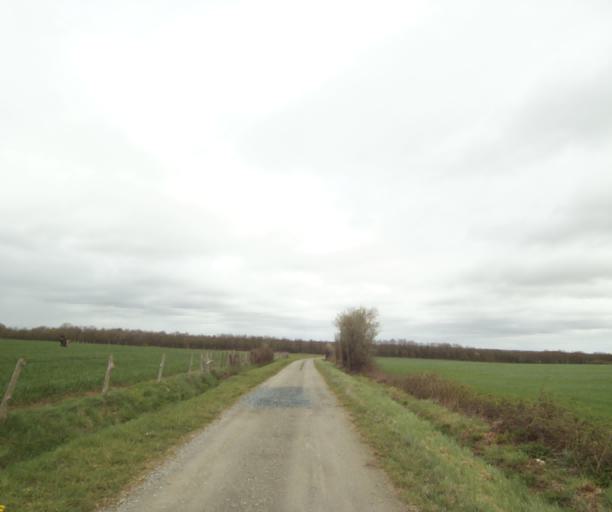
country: FR
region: Pays de la Loire
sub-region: Departement de la Loire-Atlantique
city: Bouvron
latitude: 47.4233
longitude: -1.8457
